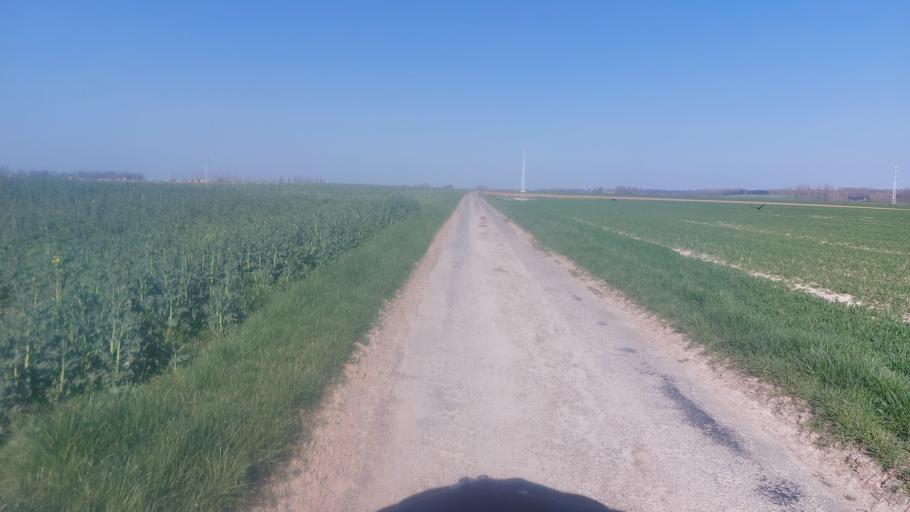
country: BE
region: Wallonia
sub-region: Province du Hainaut
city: Brugelette
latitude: 50.5950
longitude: 3.8793
